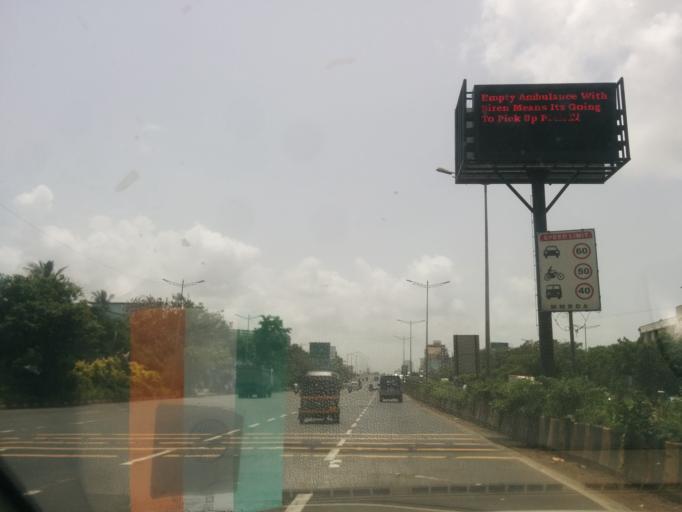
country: IN
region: Maharashtra
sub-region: Mumbai Suburban
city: Mumbai
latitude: 19.0644
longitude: 72.8466
